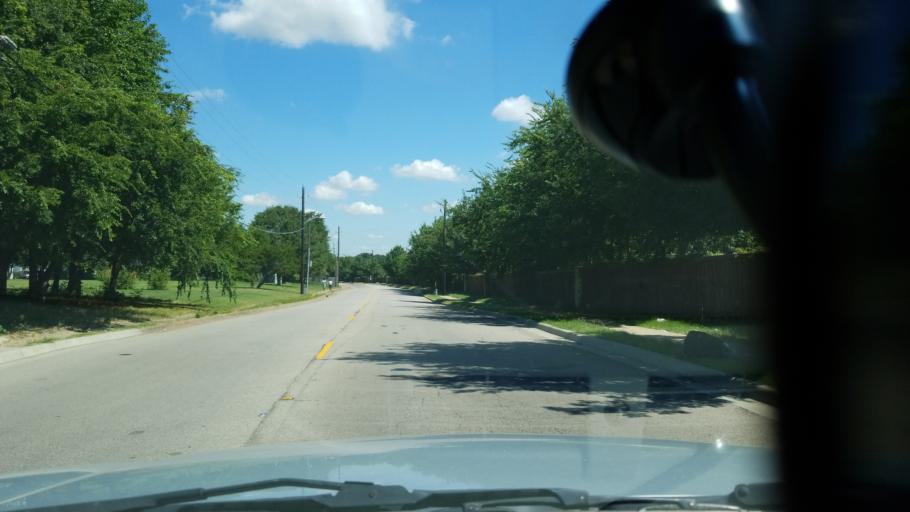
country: US
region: Texas
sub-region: Dallas County
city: Duncanville
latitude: 32.6562
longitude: -96.8669
